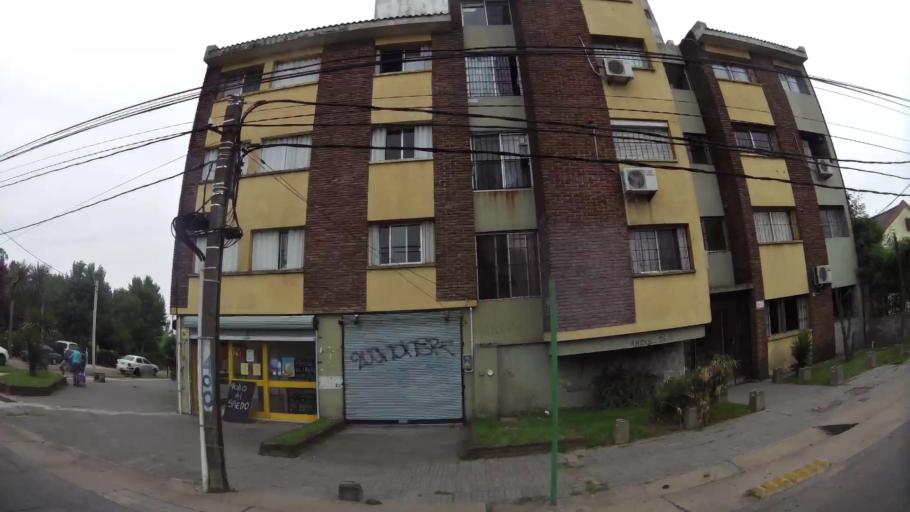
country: UY
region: Canelones
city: Las Piedras
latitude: -34.7292
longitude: -56.2277
